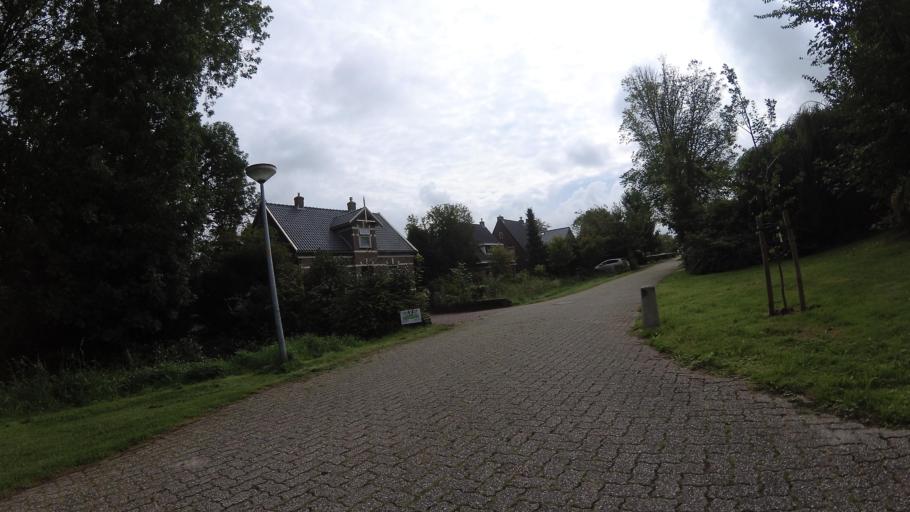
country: NL
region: North Holland
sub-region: Gemeente Schagen
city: Schagen
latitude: 52.8624
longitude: 4.8354
